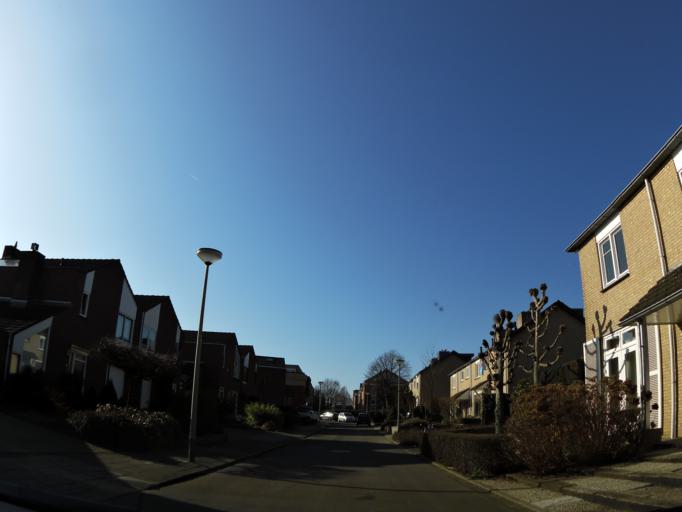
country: NL
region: Limburg
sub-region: Gemeente Kerkrade
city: Kerkrade
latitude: 50.9036
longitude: 6.0389
